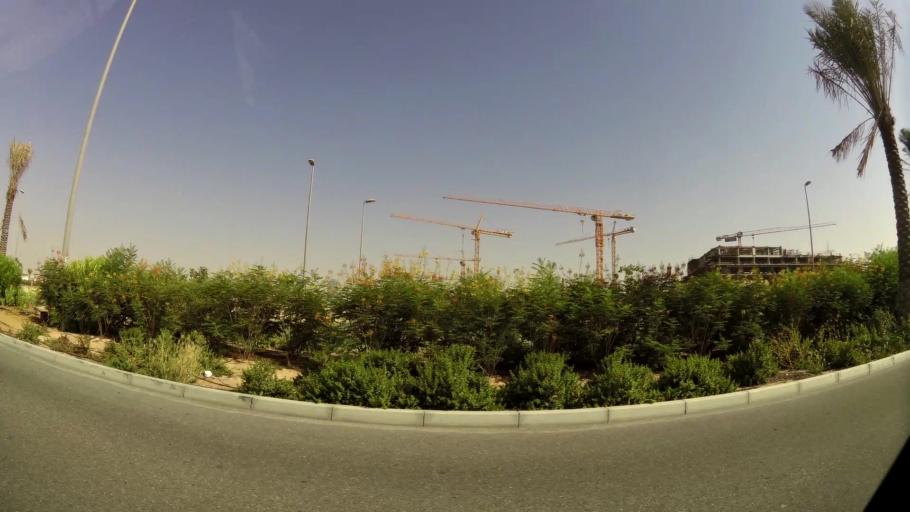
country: AE
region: Dubai
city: Dubai
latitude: 25.0683
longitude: 55.2152
